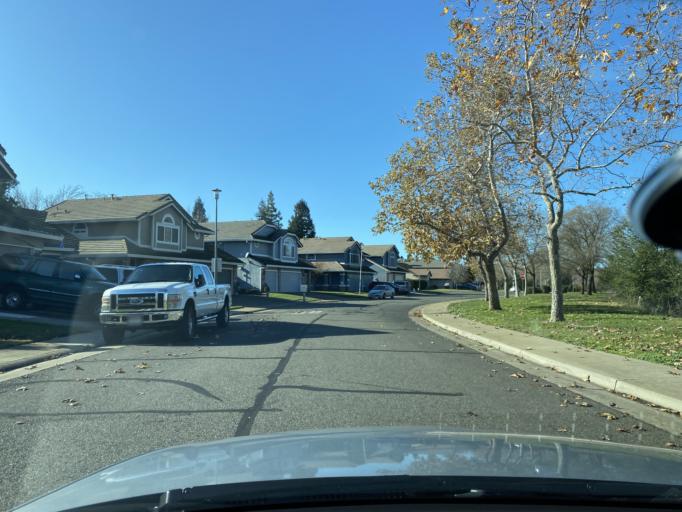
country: US
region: California
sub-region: Sacramento County
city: Elk Grove
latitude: 38.4340
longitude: -121.3821
